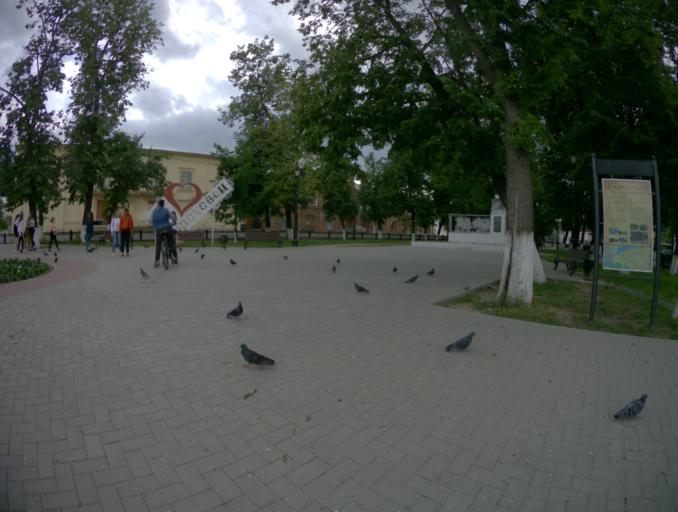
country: RU
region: Vladimir
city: Gorokhovets
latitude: 56.2066
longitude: 42.6784
